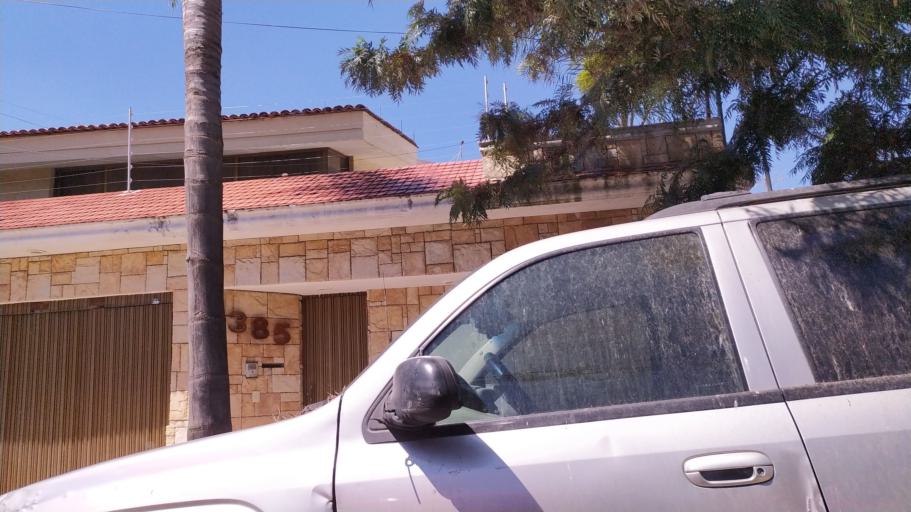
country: MX
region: Jalisco
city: Zapopan2
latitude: 20.6886
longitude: -103.4259
